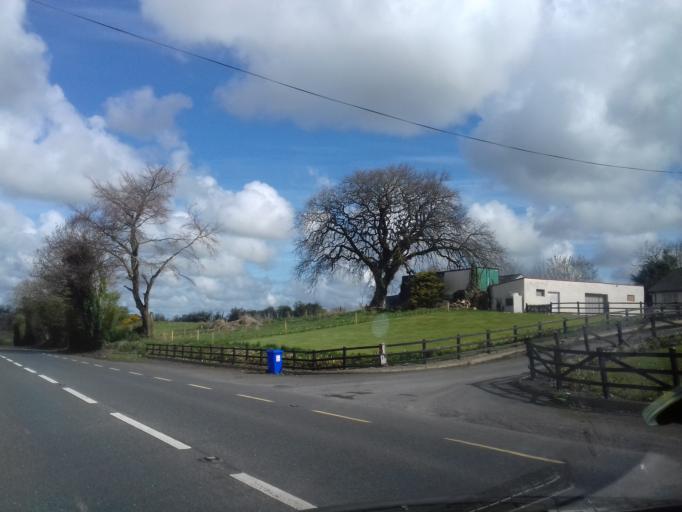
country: IE
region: Ulster
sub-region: An Cabhan
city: Ballyjamesduff
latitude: 53.9395
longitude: -7.2227
